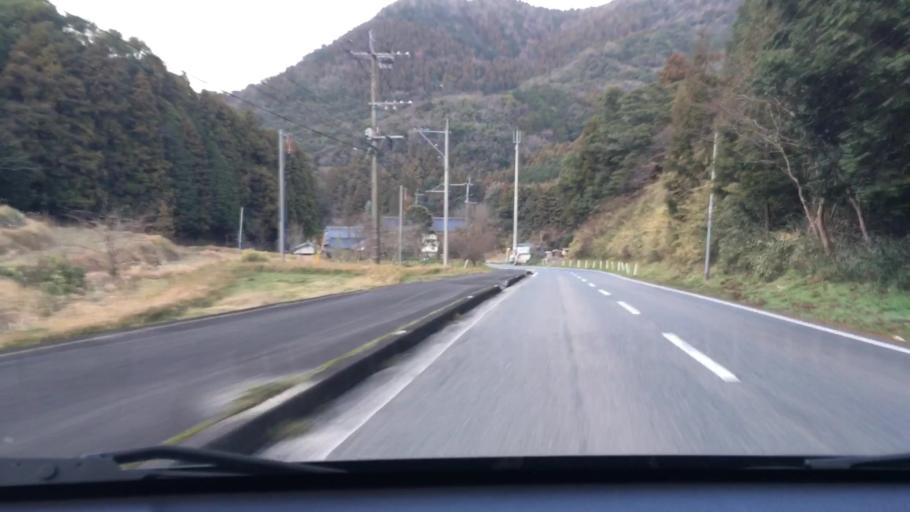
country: JP
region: Oita
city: Bungo-Takada-shi
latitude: 33.4798
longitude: 131.3864
